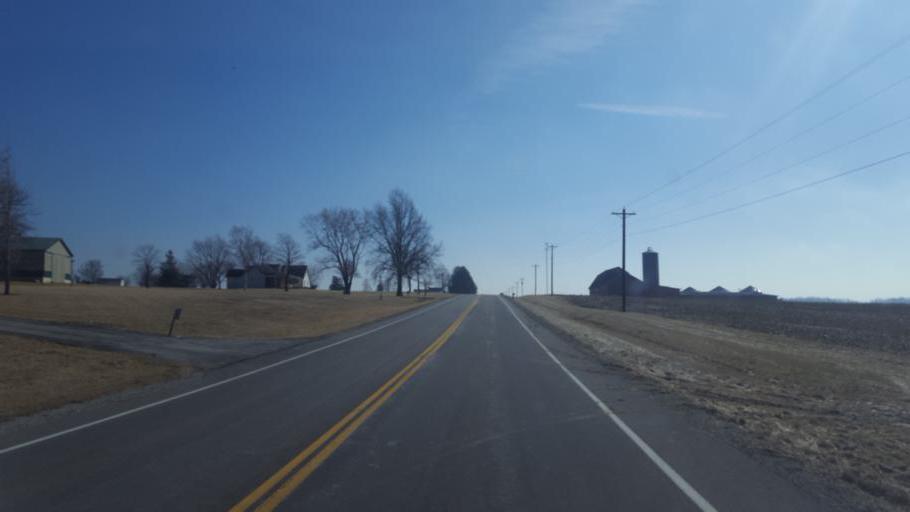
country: US
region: Ohio
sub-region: Huron County
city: Willard
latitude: 41.0588
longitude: -82.8710
